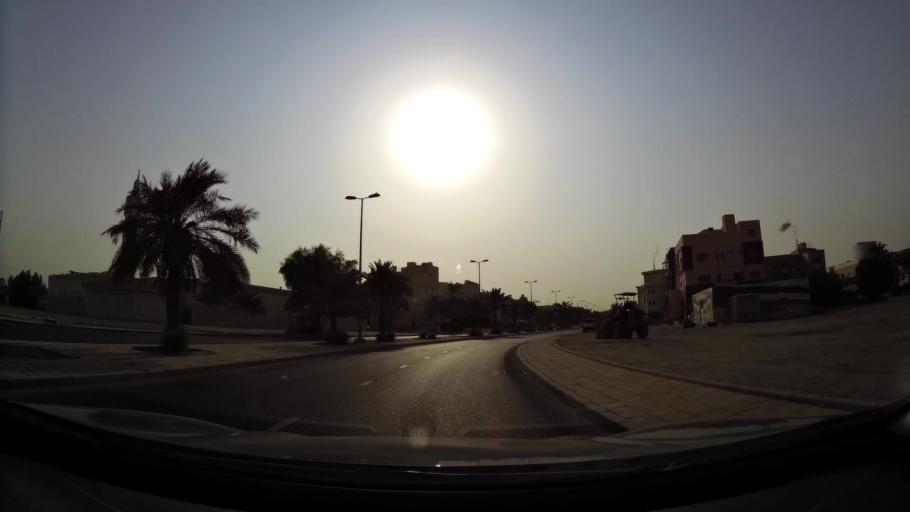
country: KW
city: Bayan
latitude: 29.3068
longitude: 48.0514
